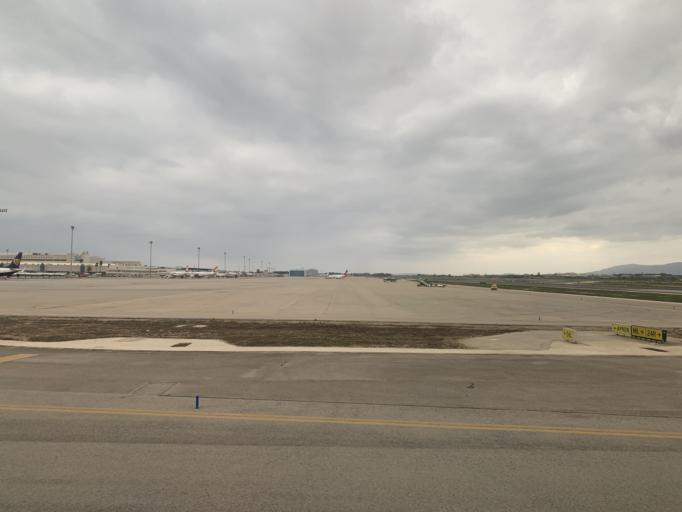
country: ES
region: Balearic Islands
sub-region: Illes Balears
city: s'Arenal
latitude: 39.5557
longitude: 2.7354
